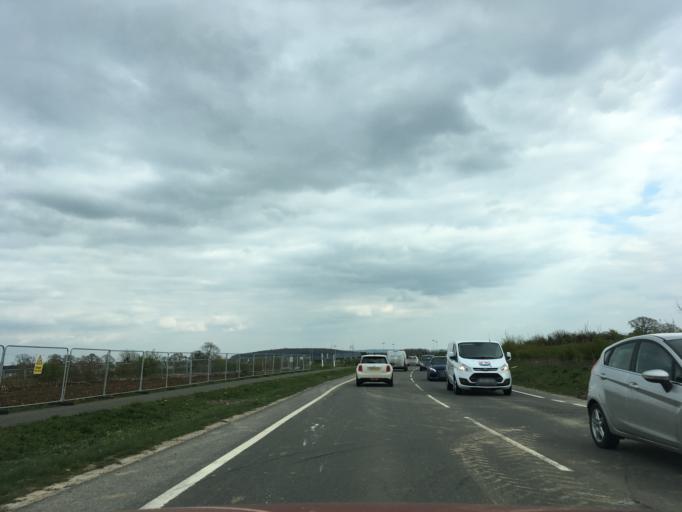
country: GB
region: England
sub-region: Oxfordshire
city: Bicester
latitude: 51.8931
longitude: -1.1790
